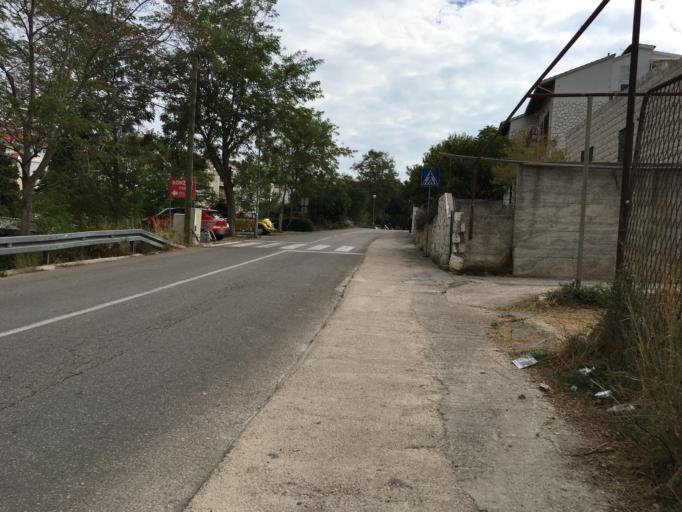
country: HR
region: Splitsko-Dalmatinska
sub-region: Grad Hvar
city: Hvar
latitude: 43.1661
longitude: 16.4466
